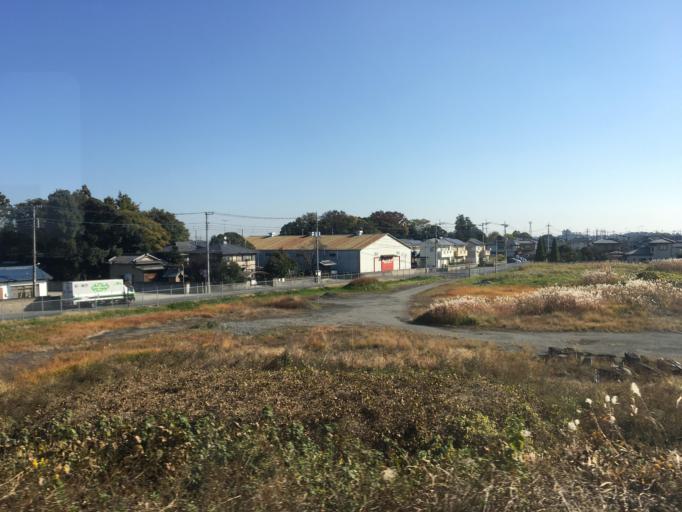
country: JP
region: Saitama
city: Hanyu
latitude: 36.1845
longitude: 139.5300
